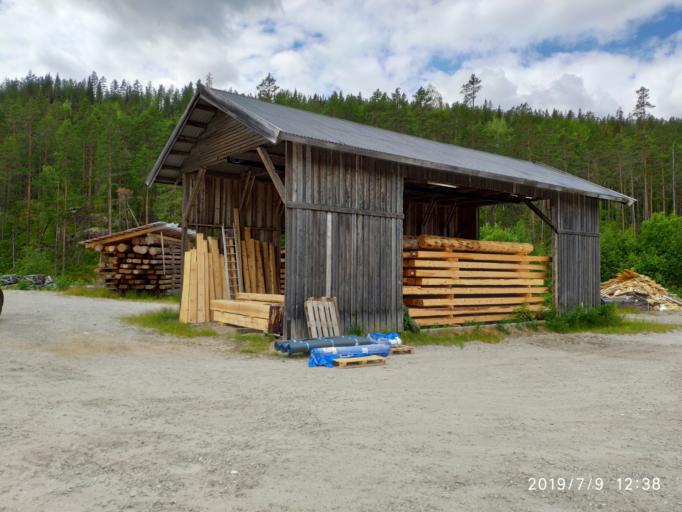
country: NO
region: Buskerud
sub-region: Fla
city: Fla
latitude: 60.2308
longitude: 9.3596
